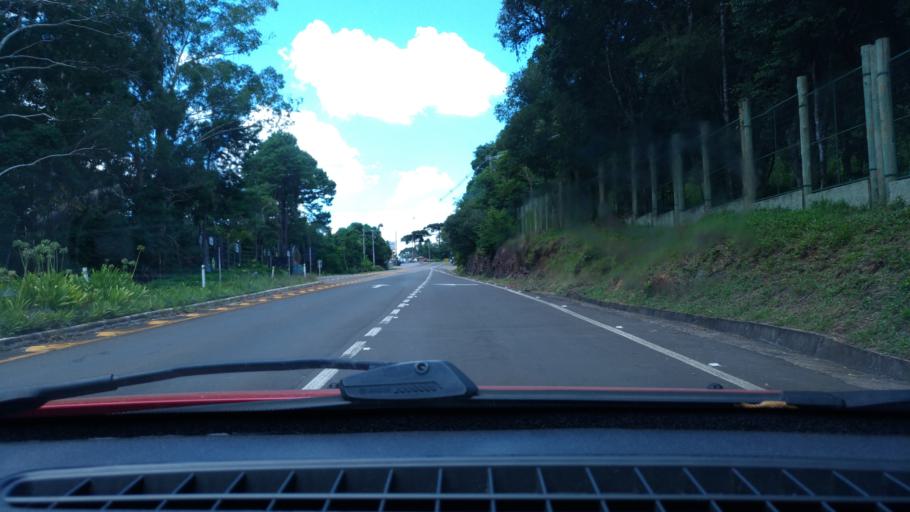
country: BR
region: Rio Grande do Sul
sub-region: Canela
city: Canela
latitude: -29.3499
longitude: -50.8355
